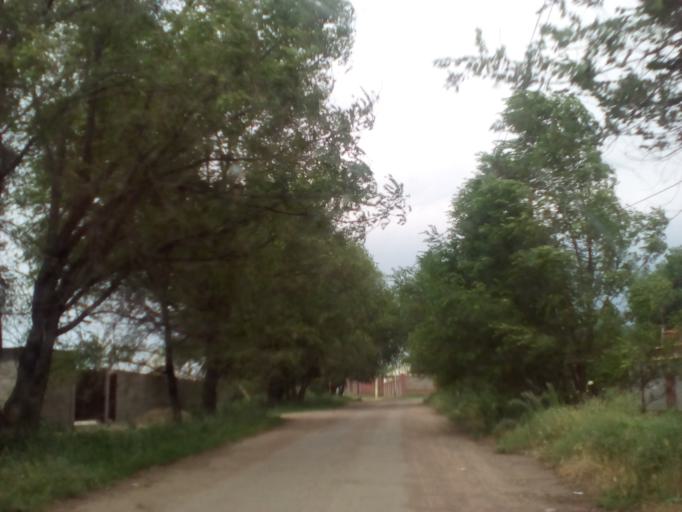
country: KZ
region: Almaty Oblysy
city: Burunday
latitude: 43.1593
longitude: 76.3963
